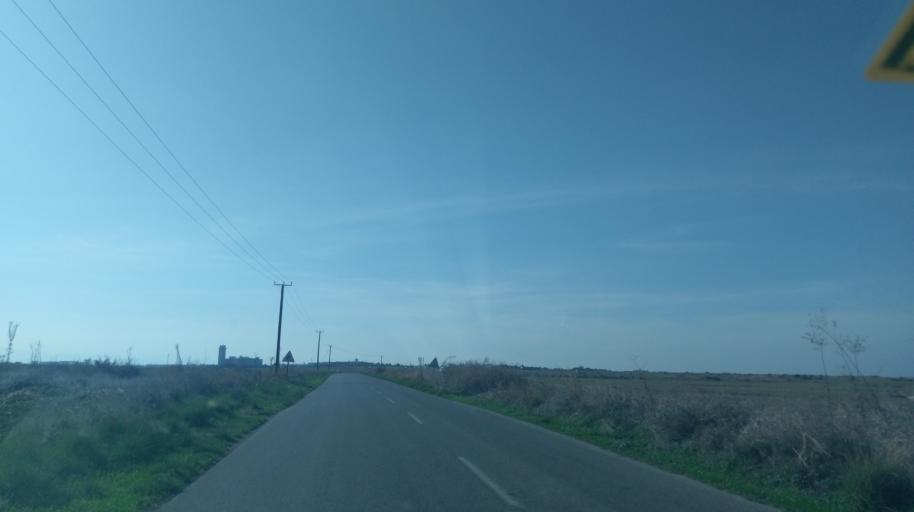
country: CY
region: Larnaka
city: Athienou
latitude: 35.1620
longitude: 33.5199
